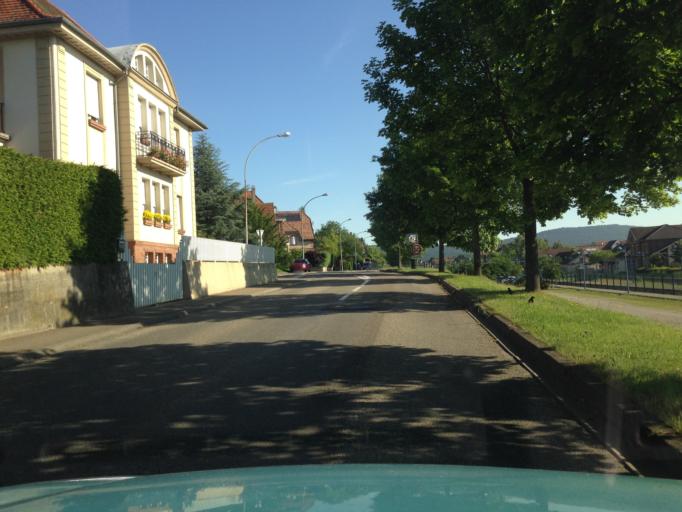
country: FR
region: Alsace
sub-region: Departement du Bas-Rhin
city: Ingwiller
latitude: 48.8706
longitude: 7.4762
